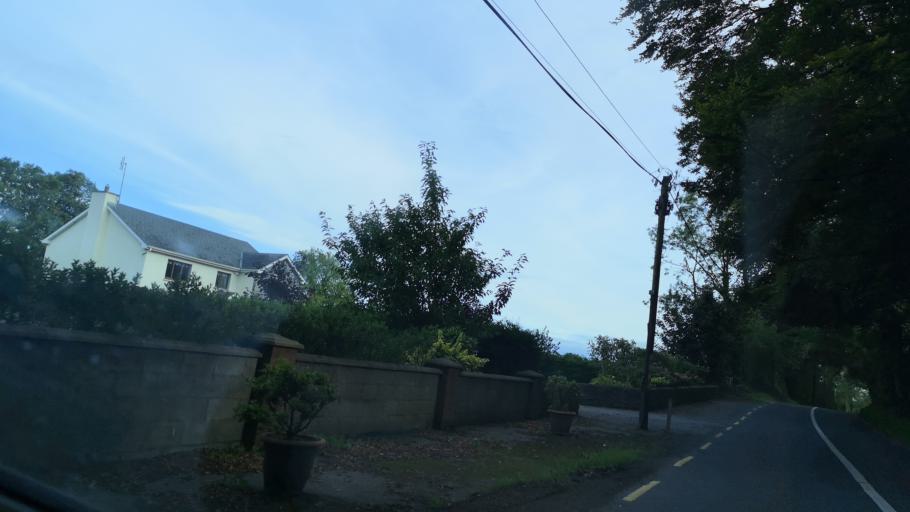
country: IE
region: Connaught
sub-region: County Galway
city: Ballinasloe
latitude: 53.3191
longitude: -8.2790
